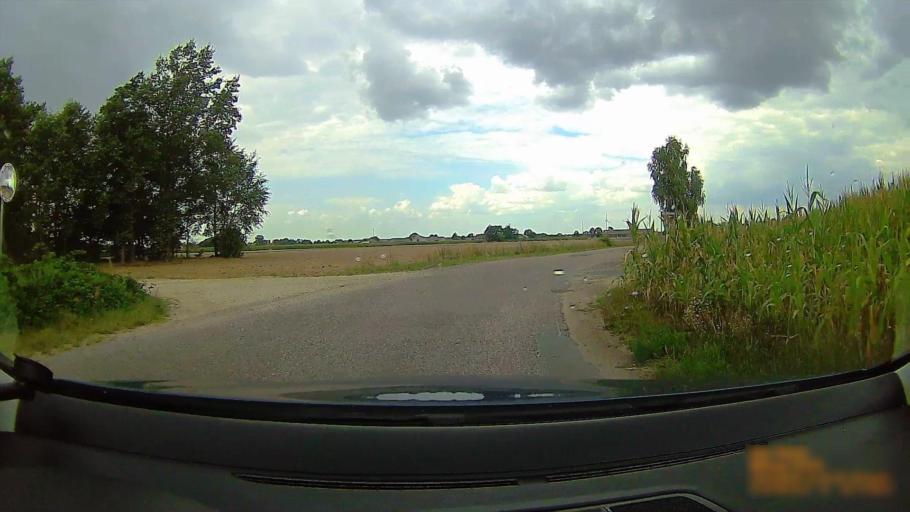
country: PL
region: Greater Poland Voivodeship
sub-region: Powiat koninski
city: Rychwal
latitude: 52.1045
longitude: 18.1913
